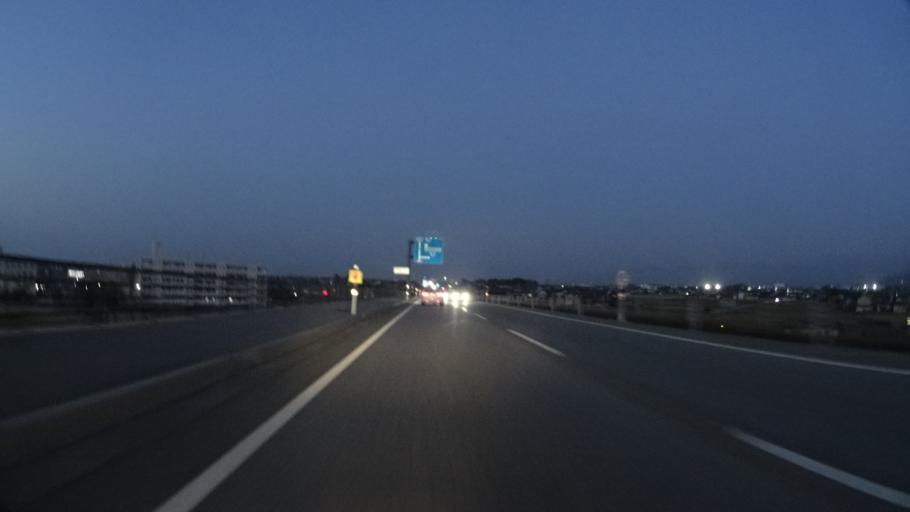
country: JP
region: Toyama
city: Uozu
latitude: 36.8803
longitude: 137.4323
